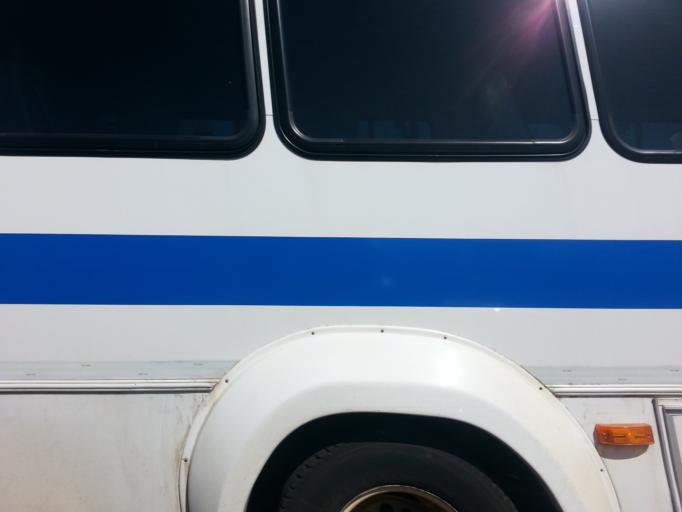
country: US
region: Wisconsin
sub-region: Dunn County
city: Menomonie
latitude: 44.8719
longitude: -91.9298
